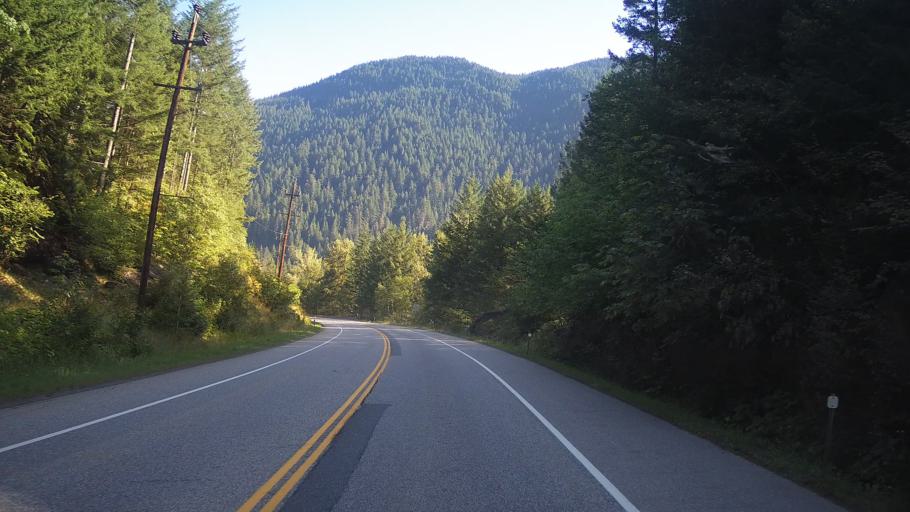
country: CA
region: British Columbia
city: Hope
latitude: 49.6274
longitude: -121.3935
